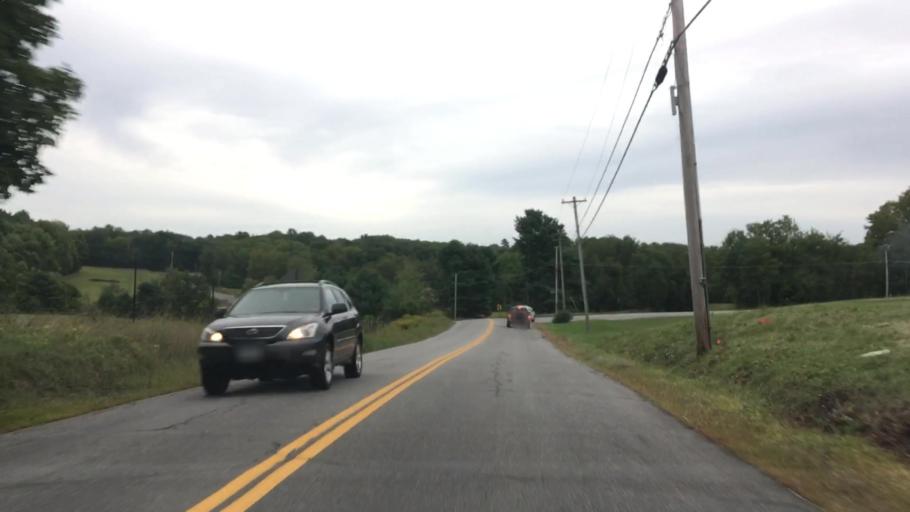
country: US
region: Maine
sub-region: Cumberland County
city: Freeport
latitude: 43.8905
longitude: -70.1807
